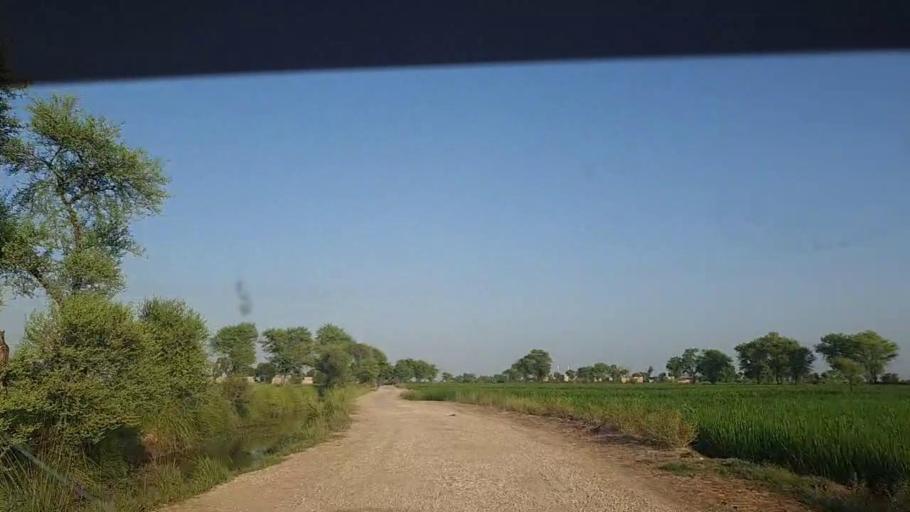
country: PK
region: Sindh
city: Thul
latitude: 28.2145
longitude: 68.8739
